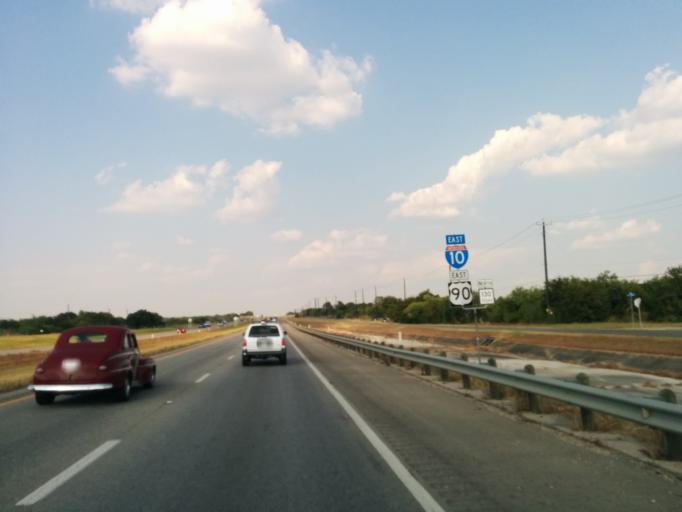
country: US
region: Texas
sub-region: Guadalupe County
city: Schertz
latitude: 29.4799
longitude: -98.2469
